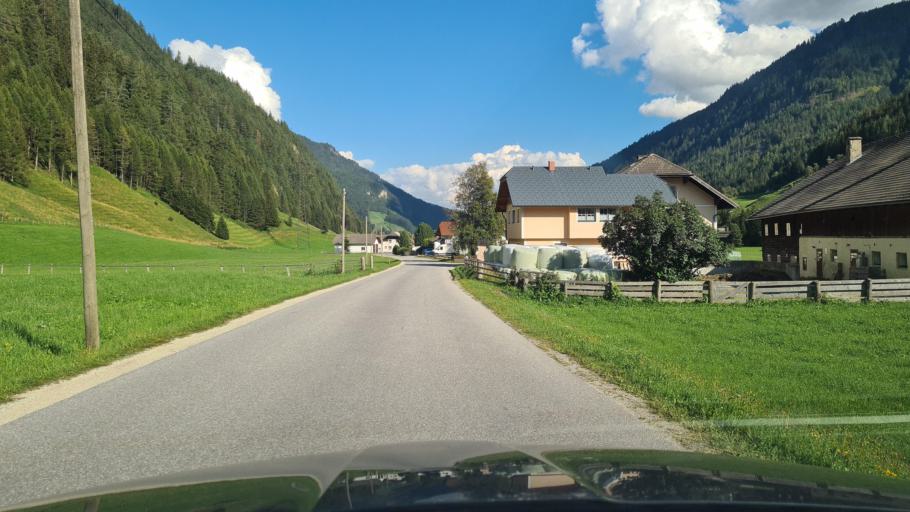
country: AT
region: Salzburg
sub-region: Politischer Bezirk Tamsweg
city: Zederhaus
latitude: 47.1663
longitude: 13.4722
